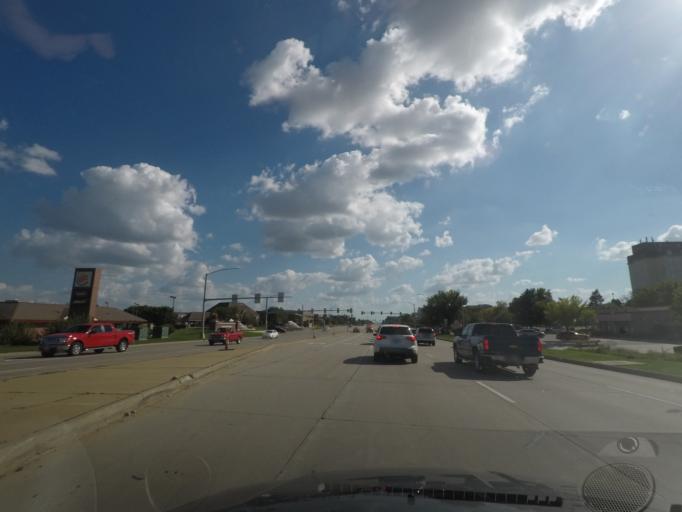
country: US
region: Iowa
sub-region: Dallas County
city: Waukee
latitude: 41.5902
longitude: -93.8092
